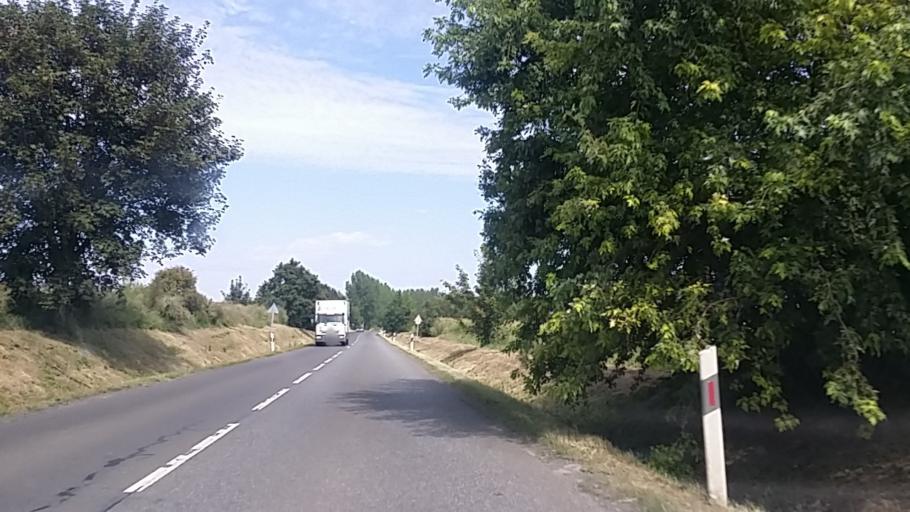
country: HU
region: Tolna
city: Dombovar
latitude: 46.3196
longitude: 18.1317
